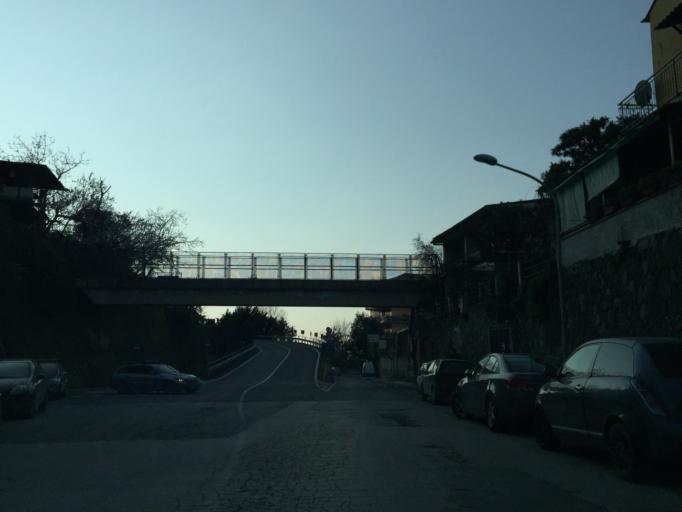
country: IT
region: Campania
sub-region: Provincia di Napoli
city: Castellammare di Stabia
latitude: 40.6874
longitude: 14.4816
